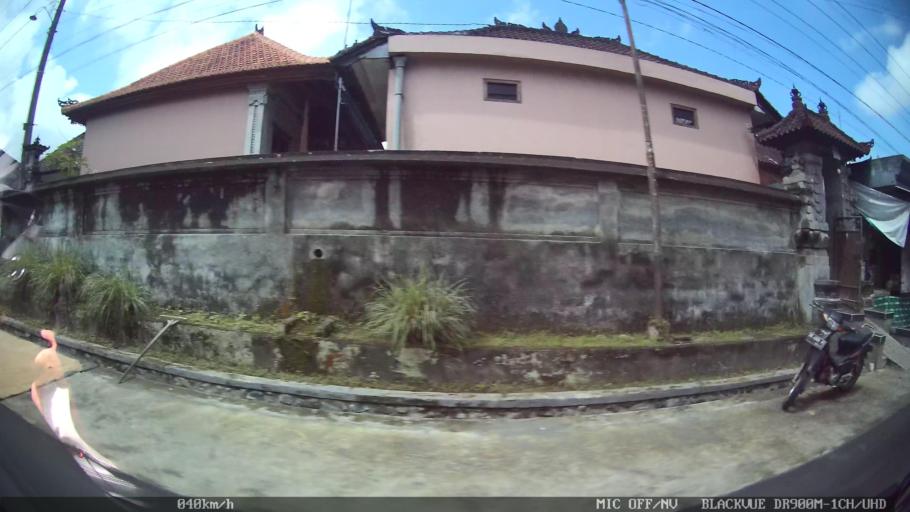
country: ID
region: Bali
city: Banjar Bebalang
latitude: -8.4794
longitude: 115.3430
